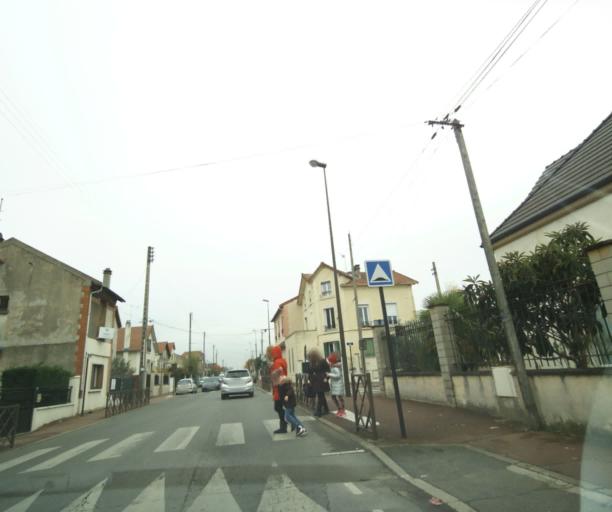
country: FR
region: Ile-de-France
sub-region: Departement de Seine-Saint-Denis
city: Le Raincy
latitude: 48.9153
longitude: 2.5208
